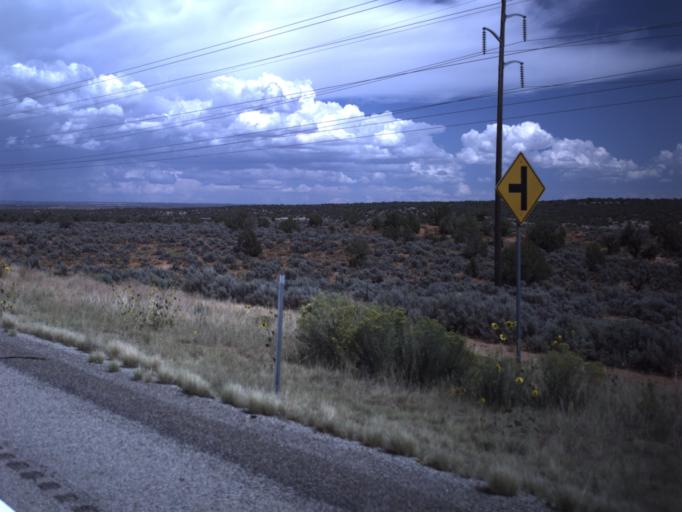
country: US
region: Utah
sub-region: San Juan County
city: Blanding
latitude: 37.5316
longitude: -109.4941
